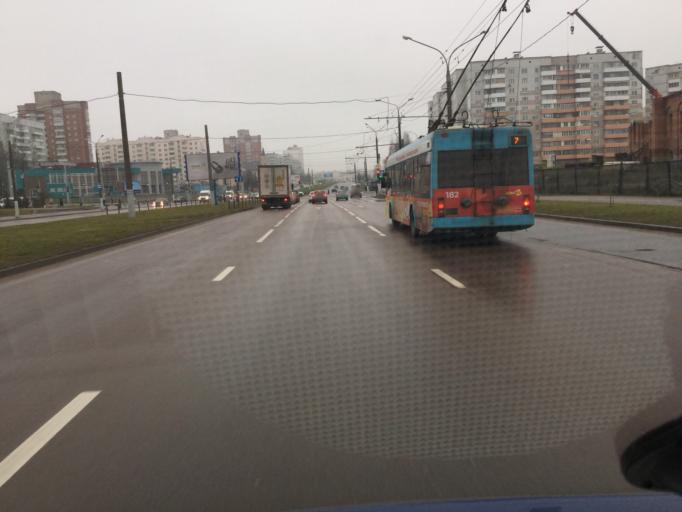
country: BY
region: Vitebsk
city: Vitebsk
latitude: 55.1637
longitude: 30.2076
